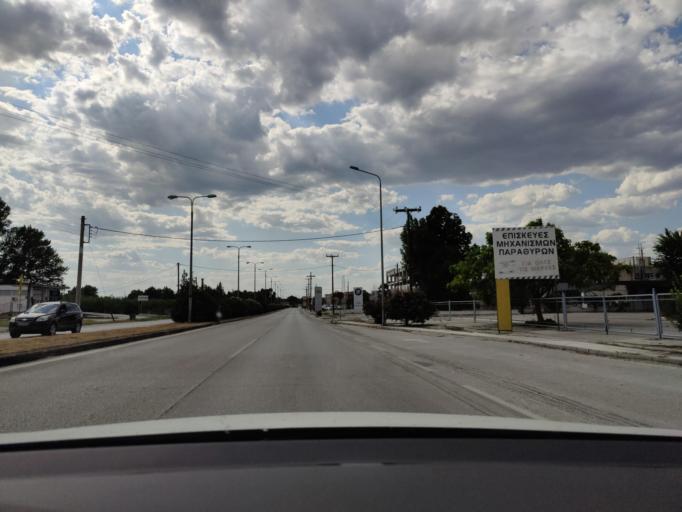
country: GR
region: Central Macedonia
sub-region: Nomos Serron
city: Lefkonas
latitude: 41.0911
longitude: 23.5148
